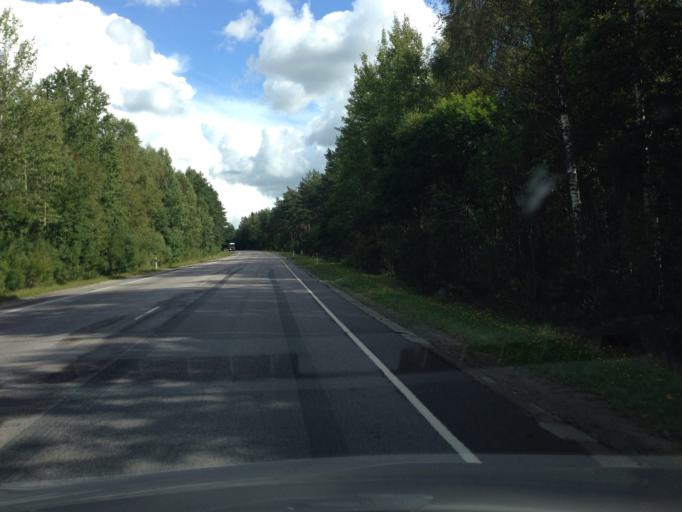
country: EE
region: Harju
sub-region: Saku vald
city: Saku
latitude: 59.3120
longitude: 24.7278
